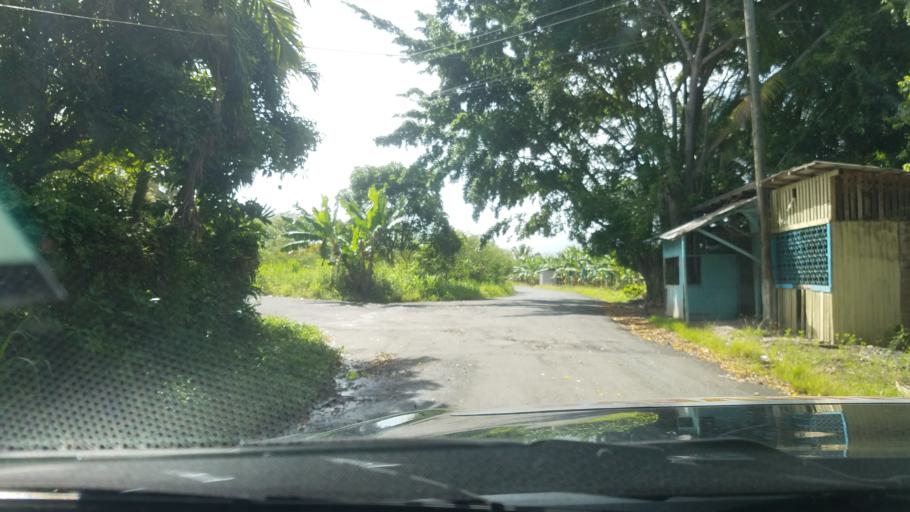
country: LC
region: Anse-la-Raye
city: Anse La Raye
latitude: 13.9570
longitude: -61.0174
